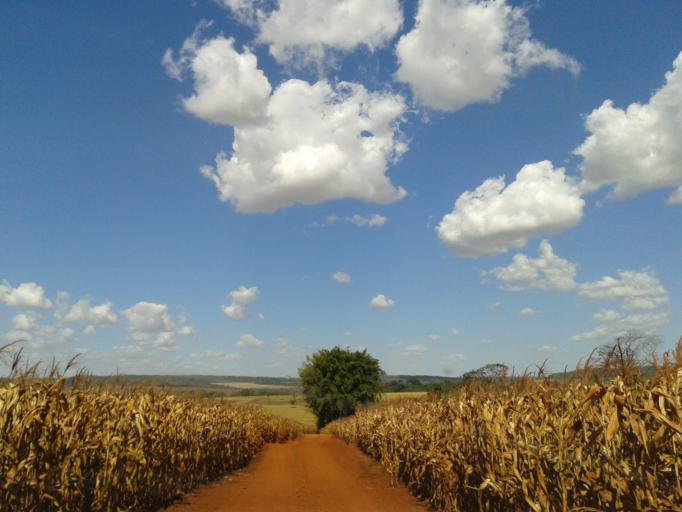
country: BR
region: Minas Gerais
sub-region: Capinopolis
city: Capinopolis
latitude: -18.6257
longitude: -49.4731
